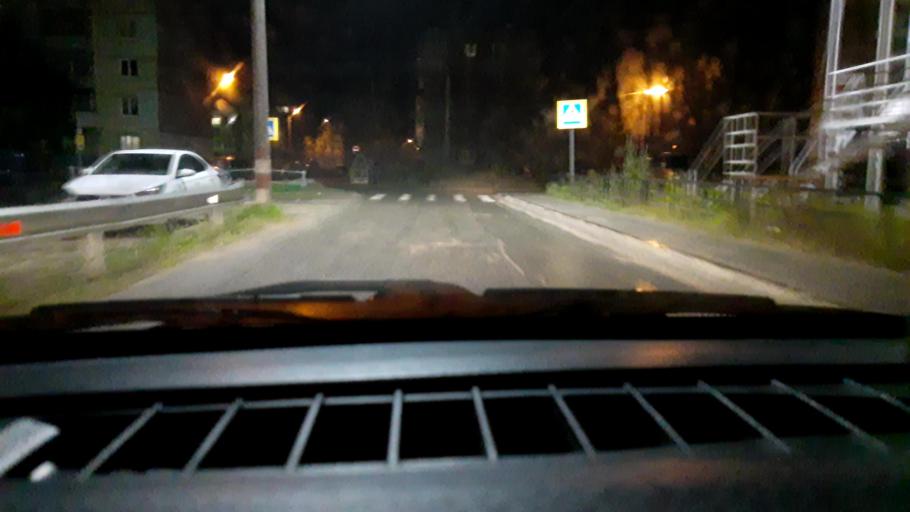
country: RU
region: Nizjnij Novgorod
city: Nizhniy Novgorod
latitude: 56.3805
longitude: 44.0214
